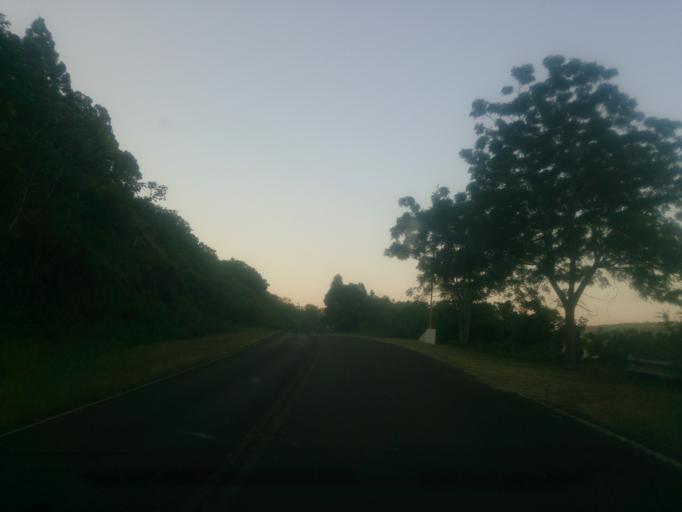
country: AR
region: Misiones
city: Panambi
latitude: -27.6829
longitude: -54.9078
